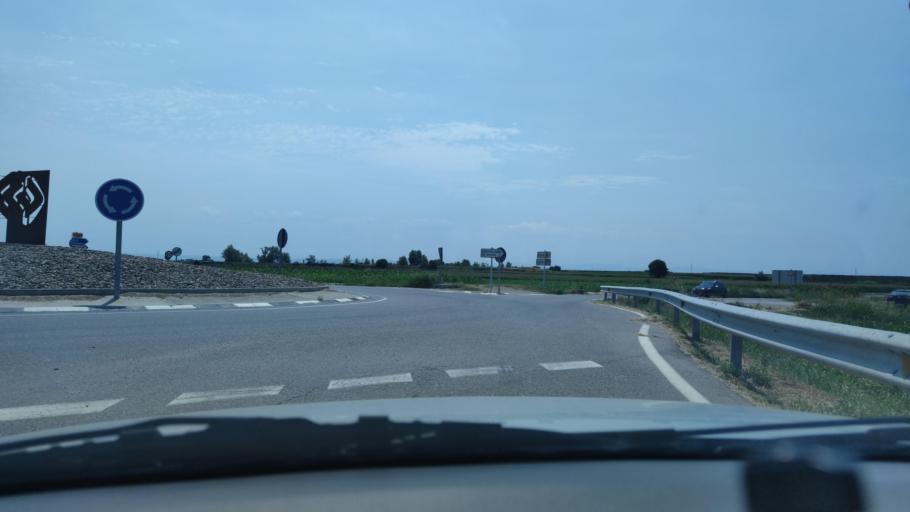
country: ES
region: Catalonia
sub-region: Provincia de Lleida
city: Ivars d'Urgell
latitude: 41.6756
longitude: 0.9832
